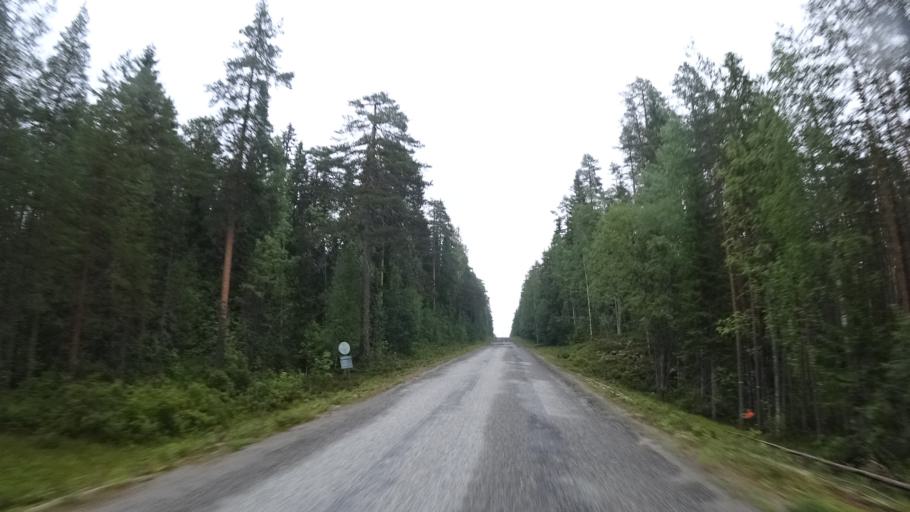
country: FI
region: North Karelia
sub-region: Joensuu
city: Ilomantsi
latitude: 63.2278
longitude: 30.8424
